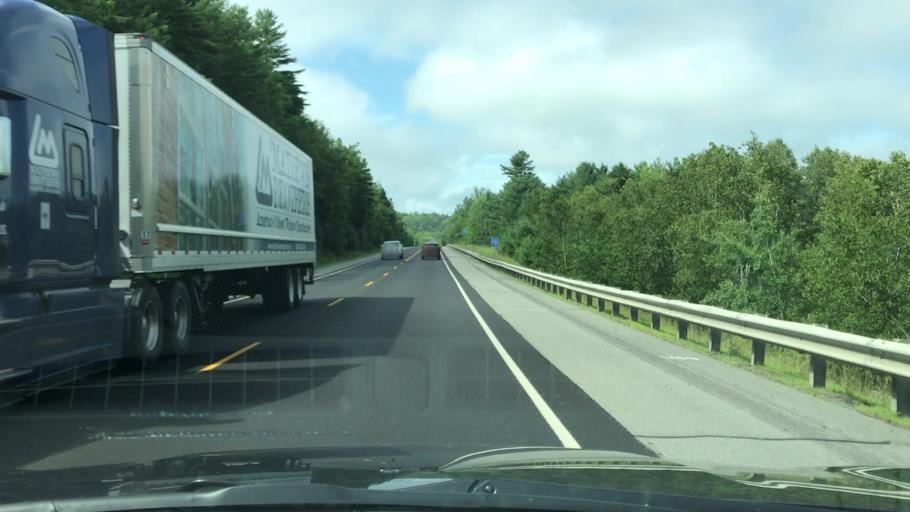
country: US
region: Maine
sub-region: Hancock County
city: Bucksport
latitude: 44.5482
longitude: -68.8093
